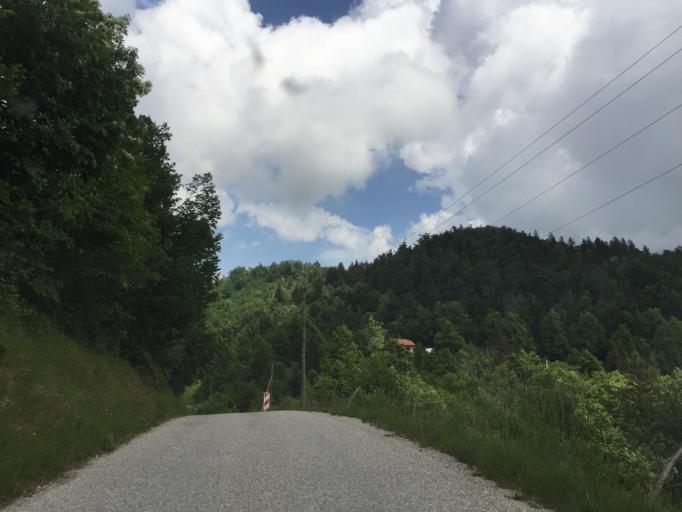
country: SI
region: Nova Gorica
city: Sempas
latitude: 46.0343
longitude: 13.7628
